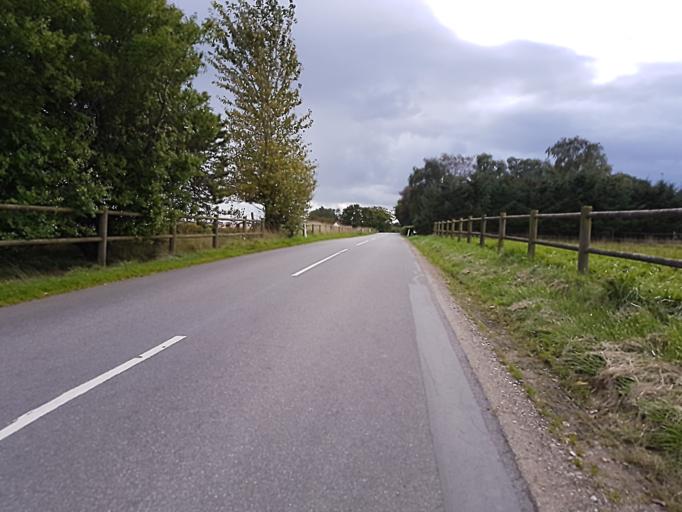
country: DK
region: Zealand
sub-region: Roskilde Kommune
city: Gundsomagle
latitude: 55.7299
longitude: 12.1424
